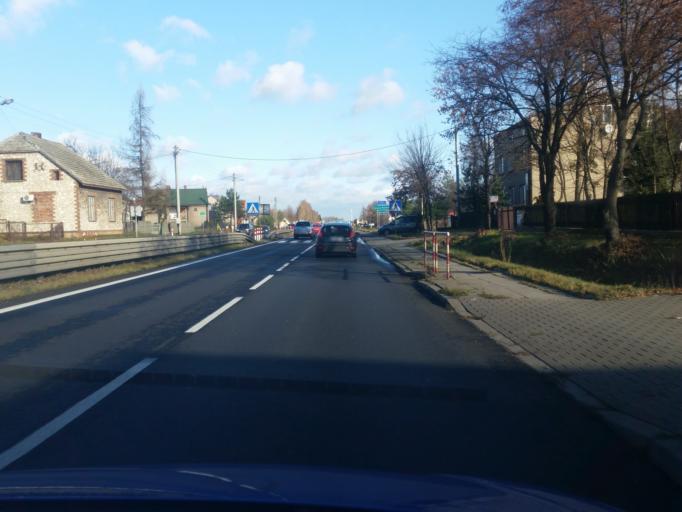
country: PL
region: Silesian Voivodeship
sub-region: Powiat czestochowski
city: Kamienica Polska
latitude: 50.6980
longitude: 19.1400
